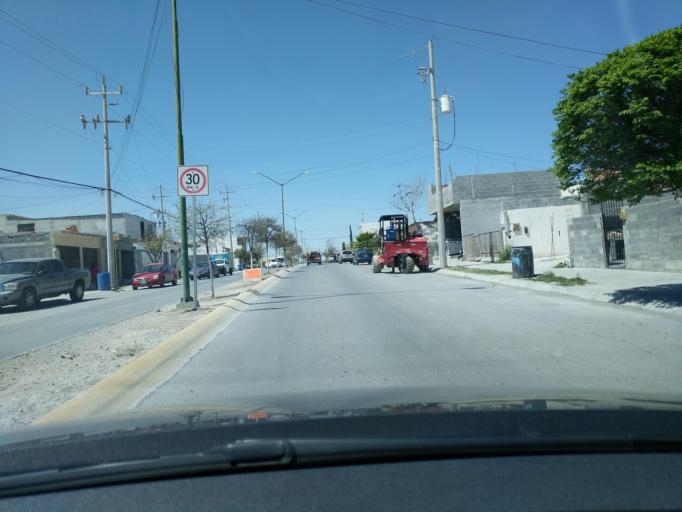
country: MX
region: Nuevo Leon
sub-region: Pesqueria
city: Colinas del Aeropuerto
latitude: 25.8238
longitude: -100.1218
